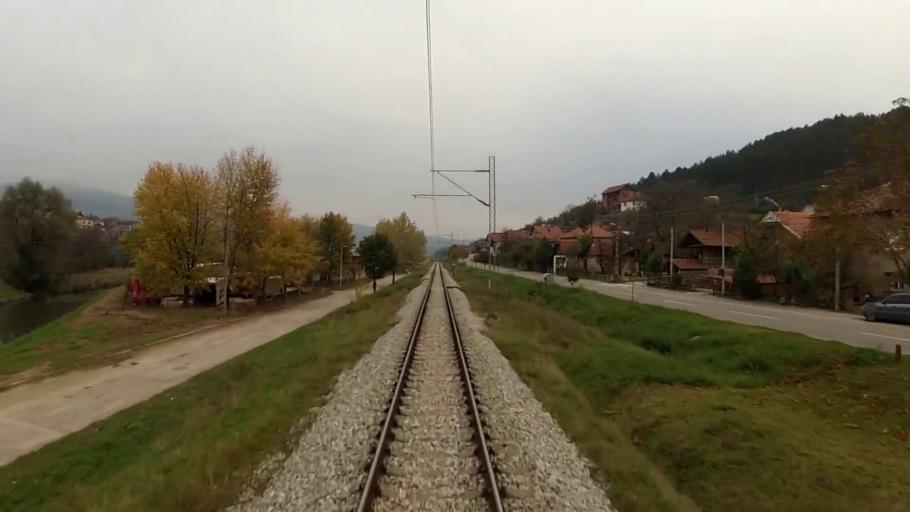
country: RS
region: Central Serbia
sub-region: Pirotski Okrug
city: Dimitrovgrad
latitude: 43.0158
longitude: 22.7906
